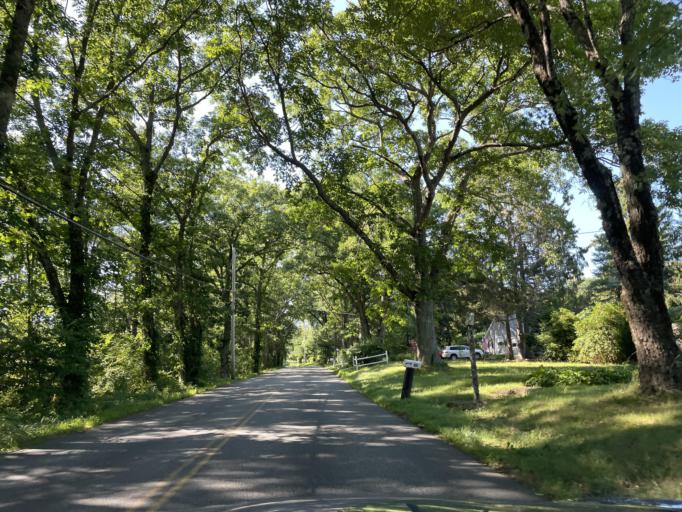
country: US
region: Massachusetts
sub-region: Worcester County
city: Charlton
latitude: 42.1643
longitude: -72.0246
